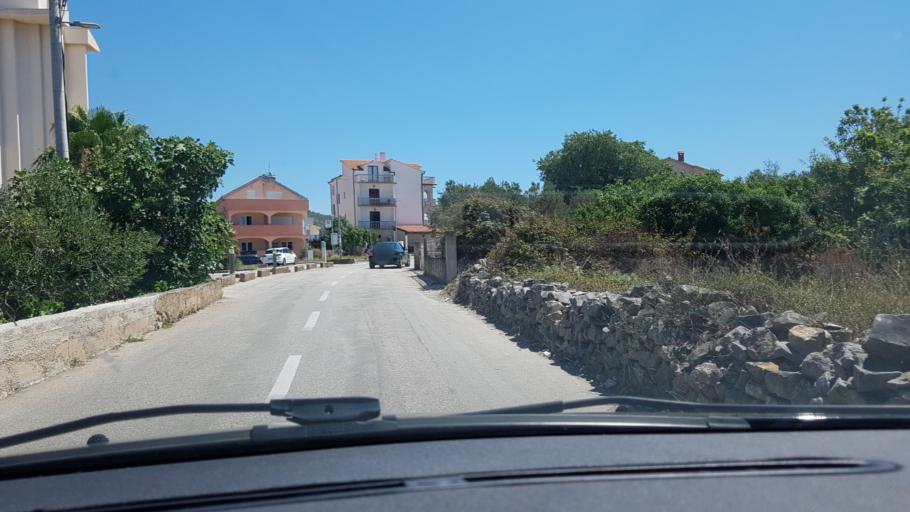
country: HR
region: Splitsko-Dalmatinska
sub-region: Grad Trogir
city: Trogir
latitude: 43.4925
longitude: 16.2643
